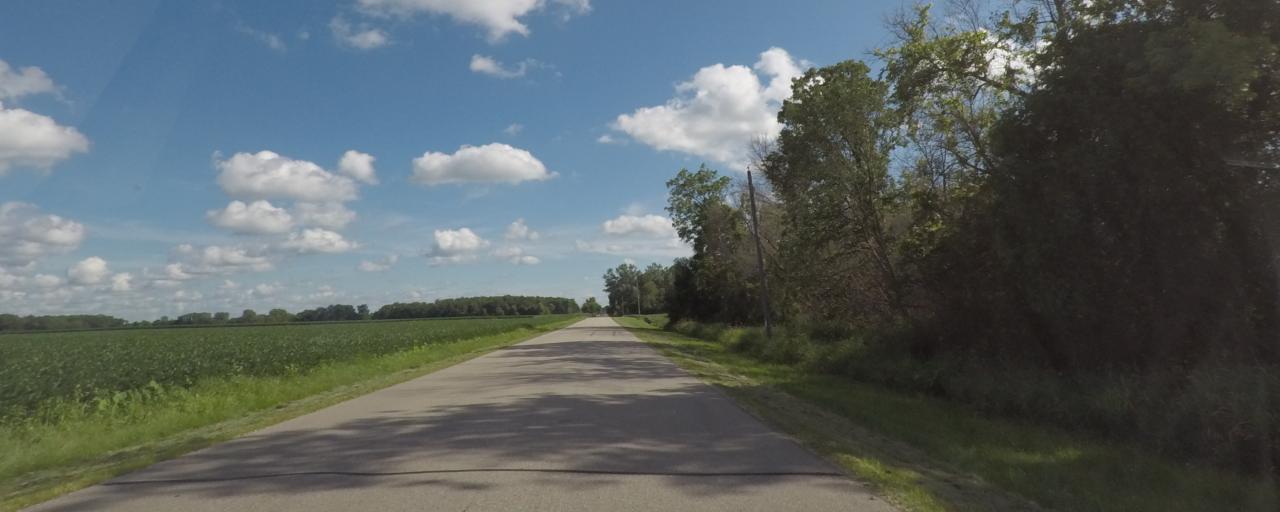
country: US
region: Wisconsin
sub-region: Dane County
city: Stoughton
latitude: 42.8972
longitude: -89.1320
